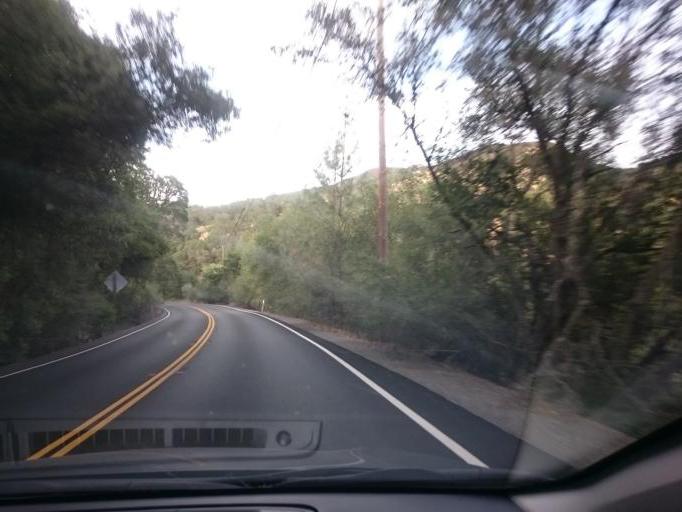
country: US
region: California
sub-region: Yolo County
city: Winters
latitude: 38.4883
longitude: -122.1278
